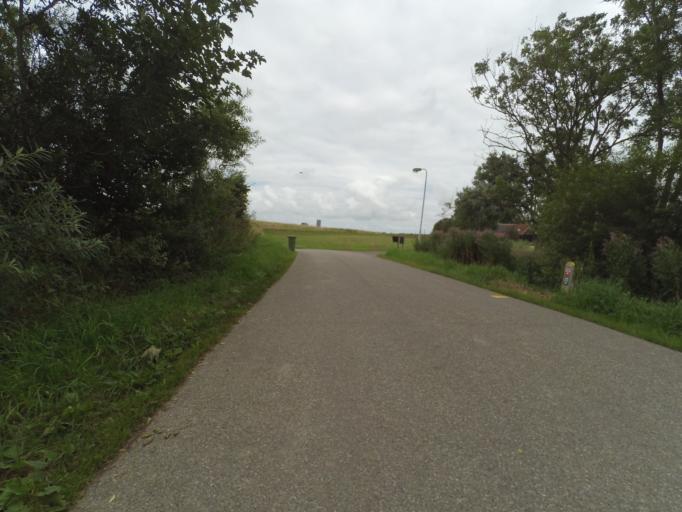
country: NL
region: Friesland
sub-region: Gemeente Dongeradeel
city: Anjum
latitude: 53.3834
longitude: 6.1328
